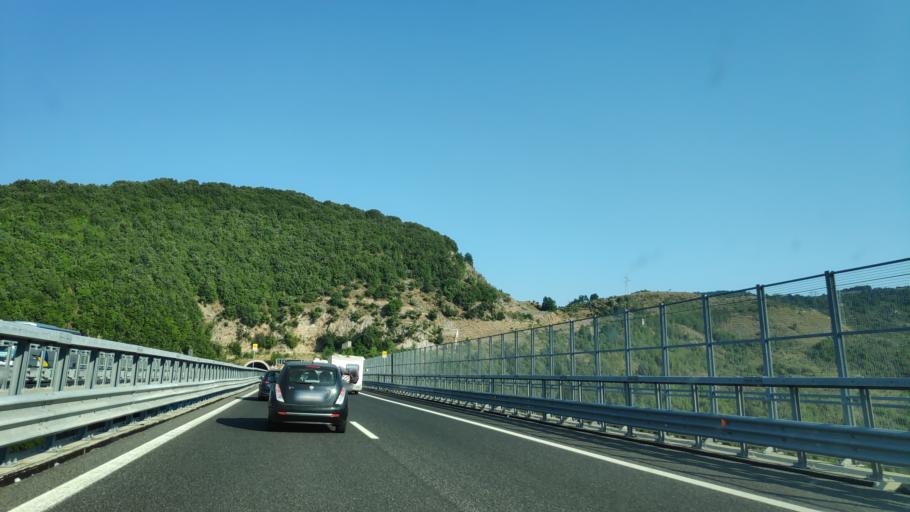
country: IT
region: Basilicate
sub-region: Provincia di Potenza
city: Lagonegro
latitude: 40.1591
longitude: 15.7374
